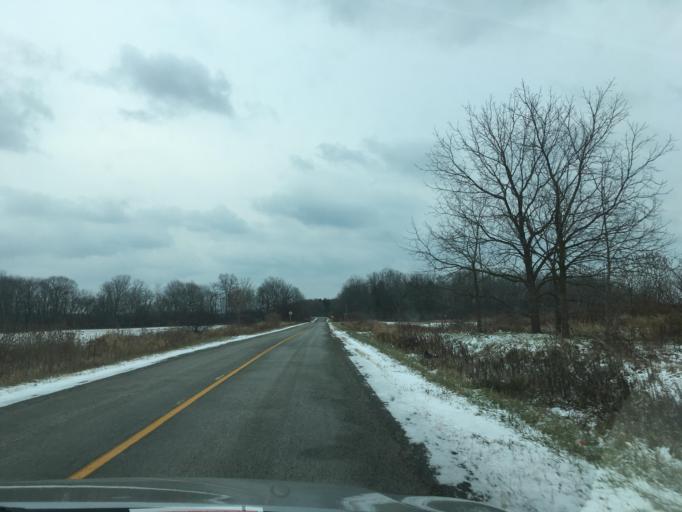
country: CA
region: Ontario
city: Norfolk County
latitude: 42.7916
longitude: -80.1198
